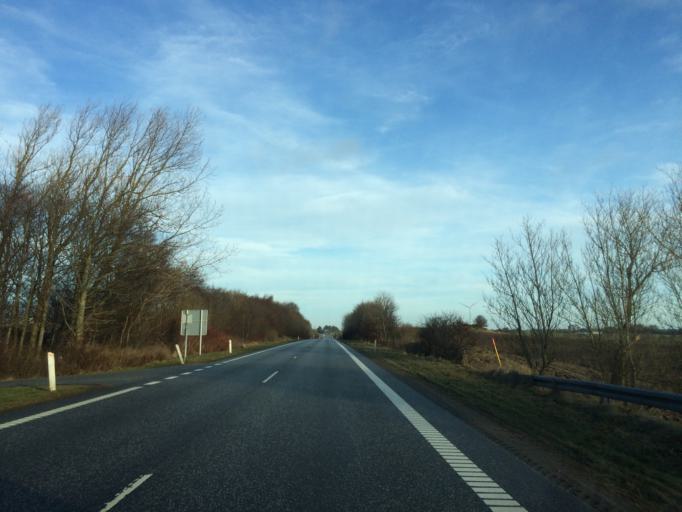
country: DK
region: North Denmark
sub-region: Thisted Kommune
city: Hurup
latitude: 56.8410
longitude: 8.5209
